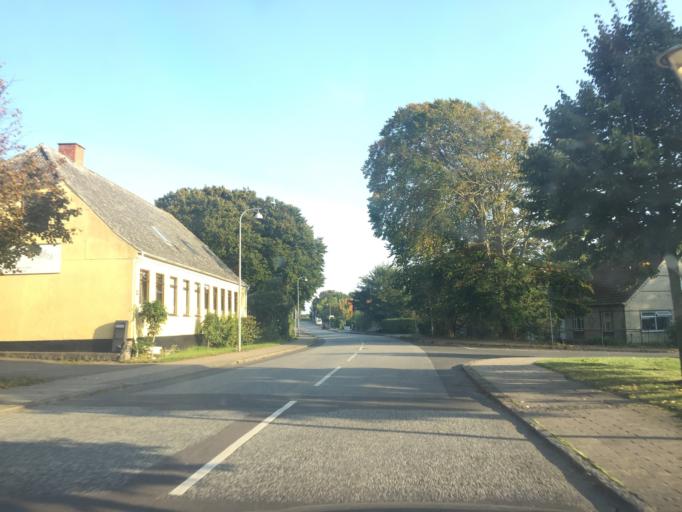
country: DK
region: Zealand
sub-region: Kalundborg Kommune
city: Svebolle
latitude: 55.6184
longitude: 11.2178
